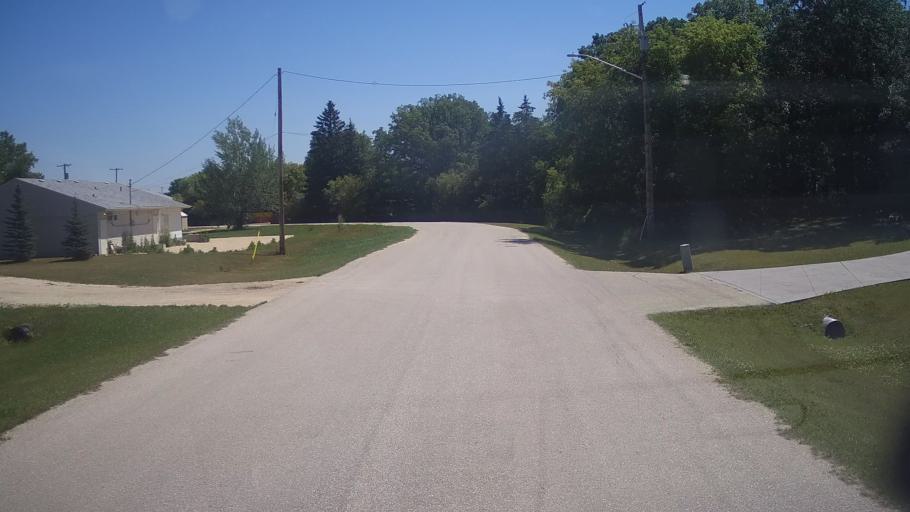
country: CA
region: Manitoba
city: Stonewall
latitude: 50.1318
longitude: -97.5479
